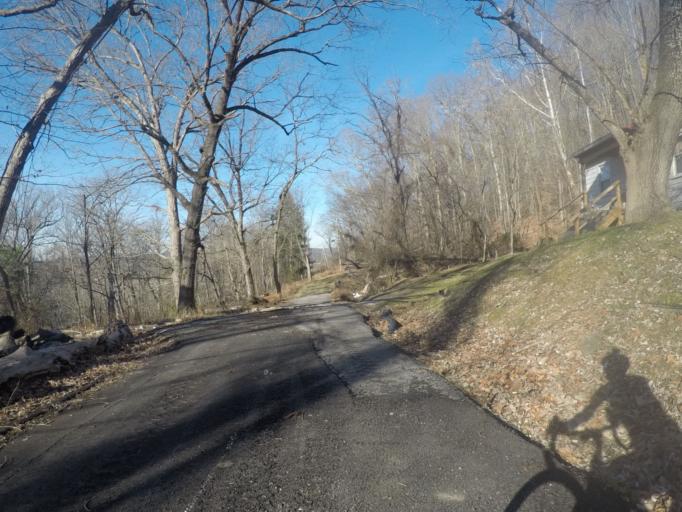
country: US
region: Ohio
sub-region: Lawrence County
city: Burlington
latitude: 38.3955
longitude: -82.4980
